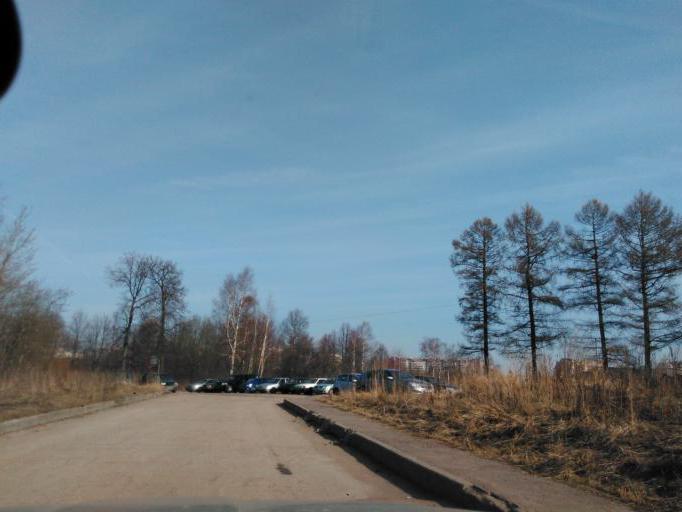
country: RU
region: Moscow
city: Zelenograd
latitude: 55.9648
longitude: 37.1625
